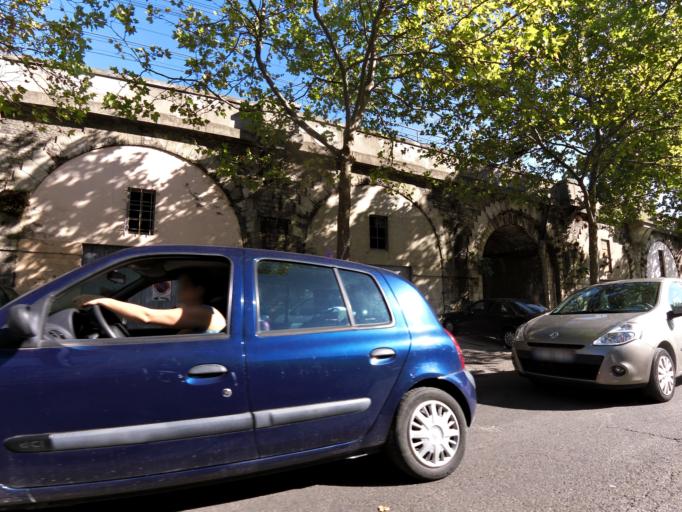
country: FR
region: Languedoc-Roussillon
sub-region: Departement du Gard
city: Nimes
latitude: 43.8363
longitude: 4.3705
